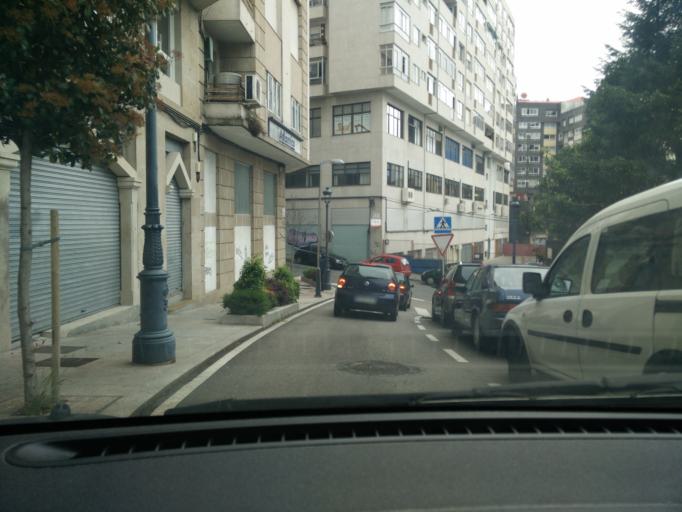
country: ES
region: Galicia
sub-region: Provincia de Pontevedra
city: Vigo
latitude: 42.2263
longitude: -8.7300
